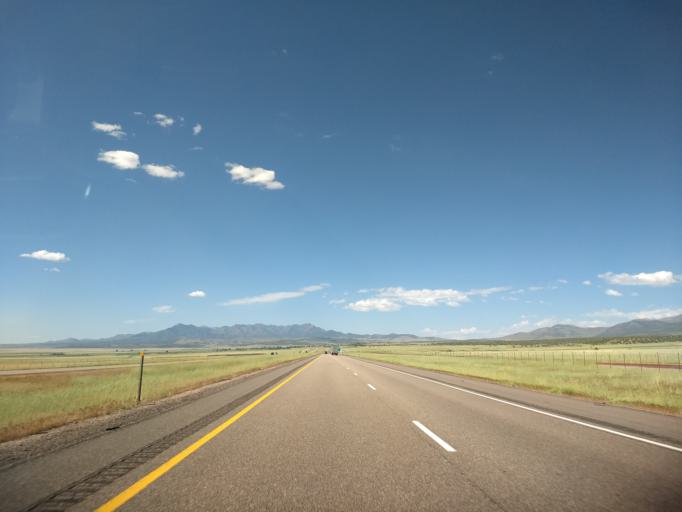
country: US
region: Utah
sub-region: Millard County
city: Fillmore
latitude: 39.0589
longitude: -112.2871
